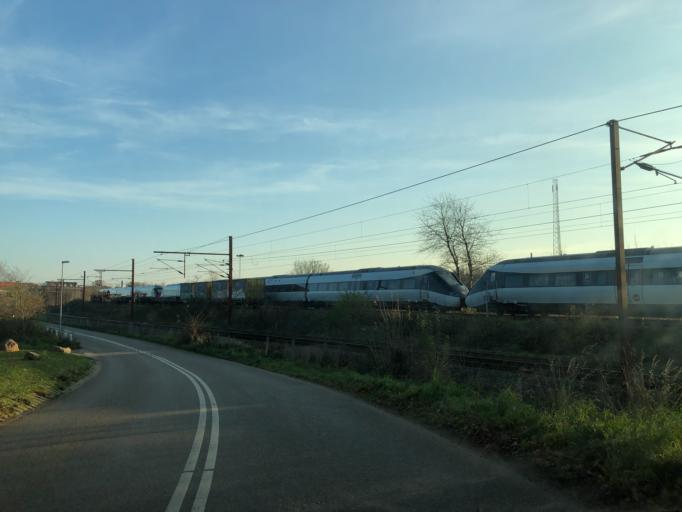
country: DK
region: South Denmark
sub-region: Fredericia Kommune
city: Fredericia
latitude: 55.5809
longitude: 9.7349
